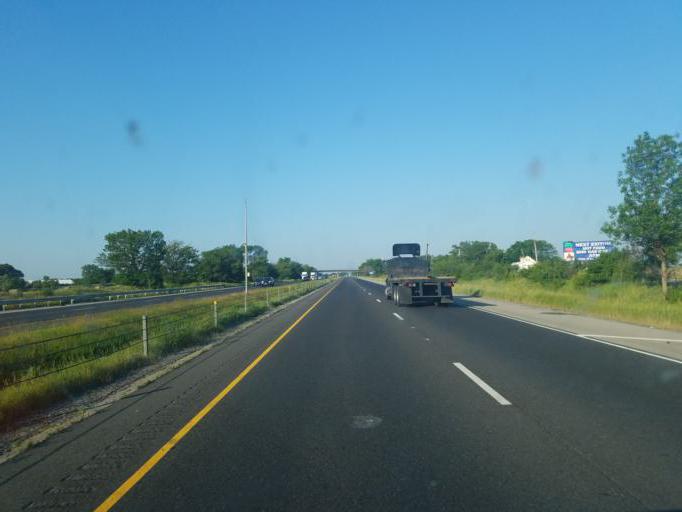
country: US
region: Illinois
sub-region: Grundy County
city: Minooka
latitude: 41.4737
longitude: -88.2379
